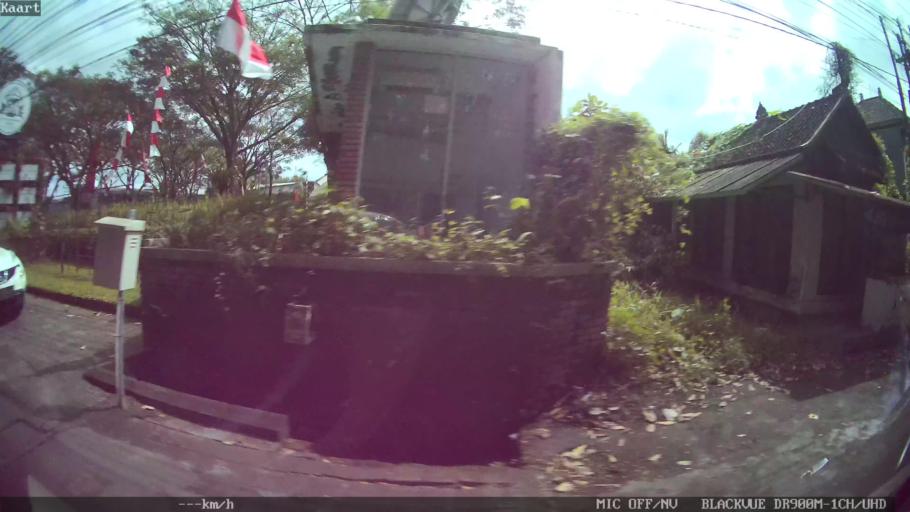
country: ID
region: Bali
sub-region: Kabupaten Gianyar
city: Ubud
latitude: -8.5230
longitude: 115.2795
